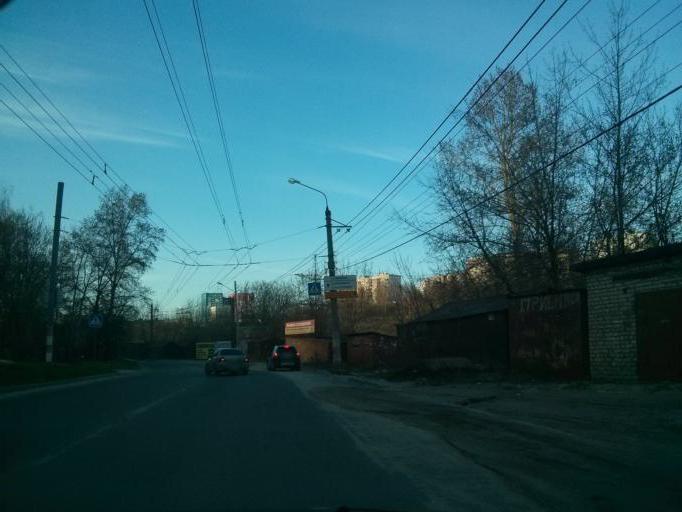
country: RU
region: Nizjnij Novgorod
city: Afonino
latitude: 56.2916
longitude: 44.0537
